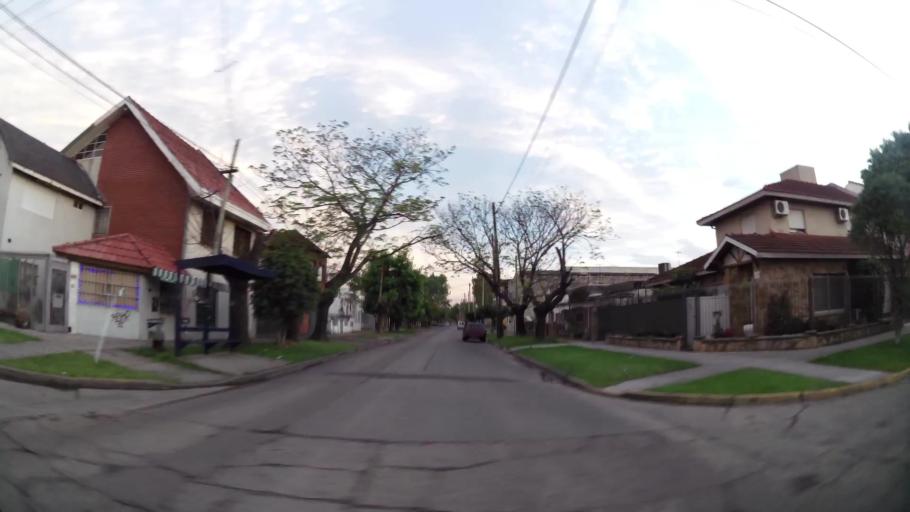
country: AR
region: Buenos Aires
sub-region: Partido de Lomas de Zamora
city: Lomas de Zamora
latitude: -34.7584
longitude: -58.3763
